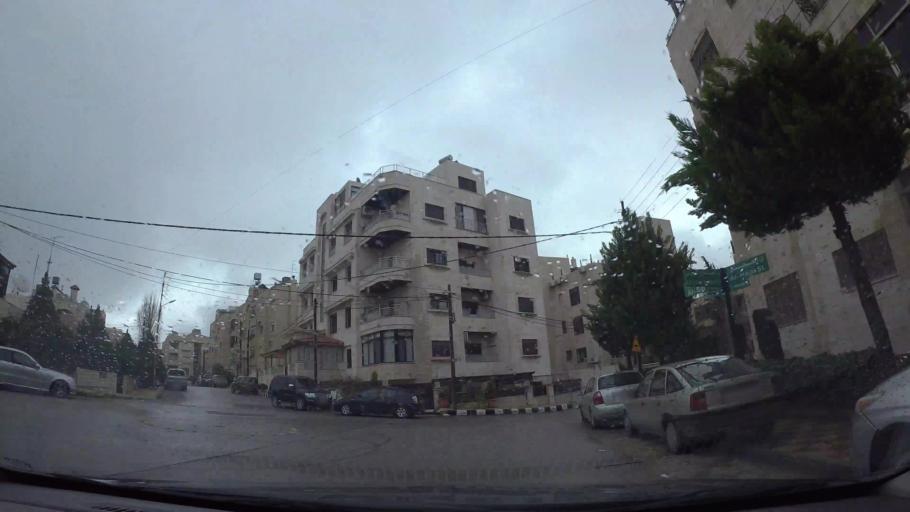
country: JO
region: Amman
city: Wadi as Sir
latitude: 31.9649
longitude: 35.8484
